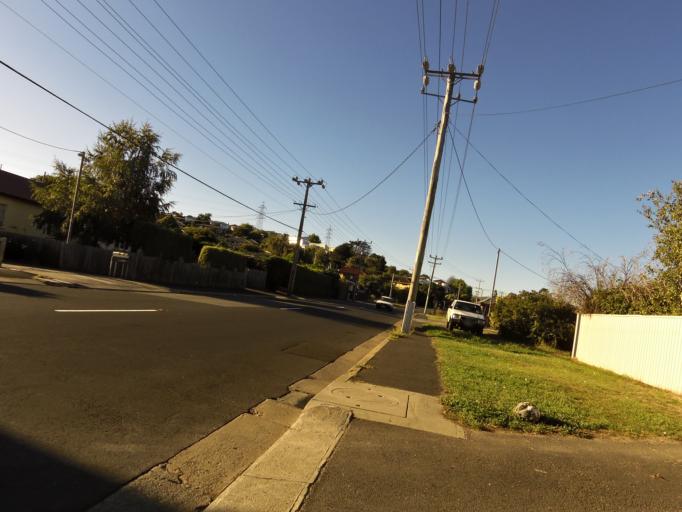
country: AU
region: Tasmania
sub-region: Hobart
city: New Town
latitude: -42.8475
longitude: 147.3134
